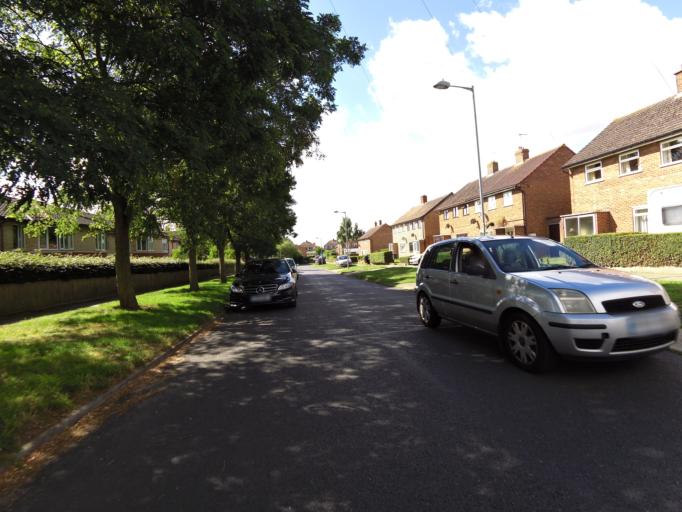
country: GB
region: England
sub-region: Suffolk
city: Ipswich
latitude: 52.0812
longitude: 1.1384
